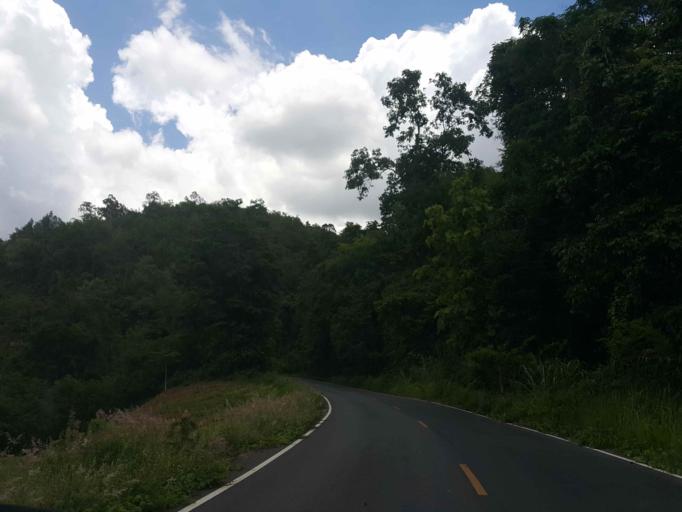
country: TH
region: Nan
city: Wiang Sa
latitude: 18.5351
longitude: 100.5490
